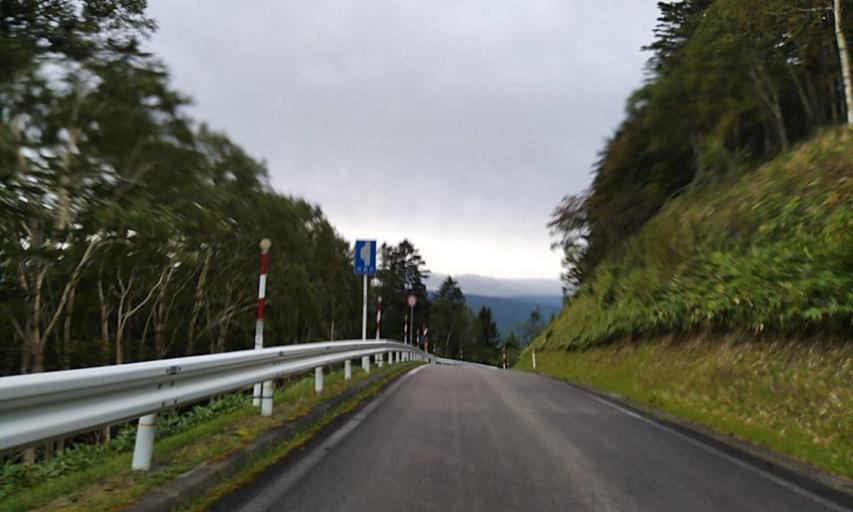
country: JP
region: Hokkaido
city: Bihoro
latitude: 43.5651
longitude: 144.2225
